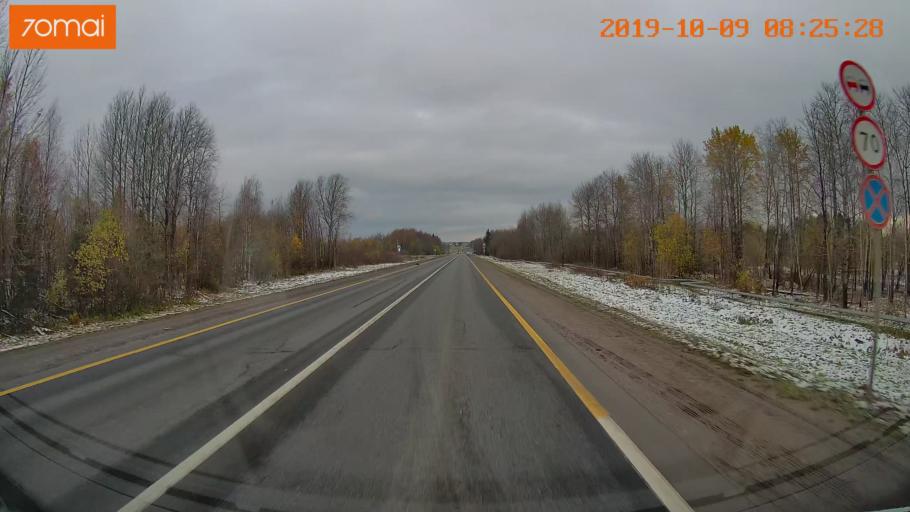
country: RU
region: Vologda
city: Gryazovets
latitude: 58.7815
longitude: 40.2721
